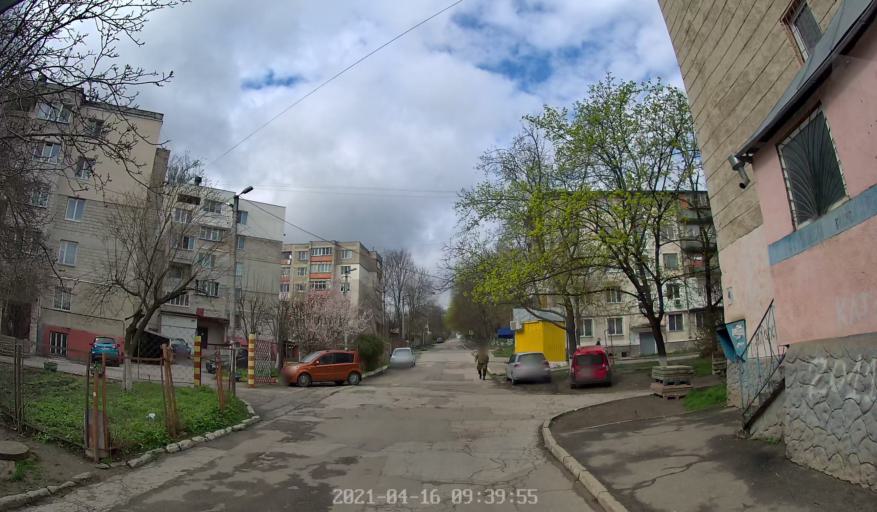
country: MD
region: Chisinau
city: Stauceni
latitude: 47.0573
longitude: 28.8461
